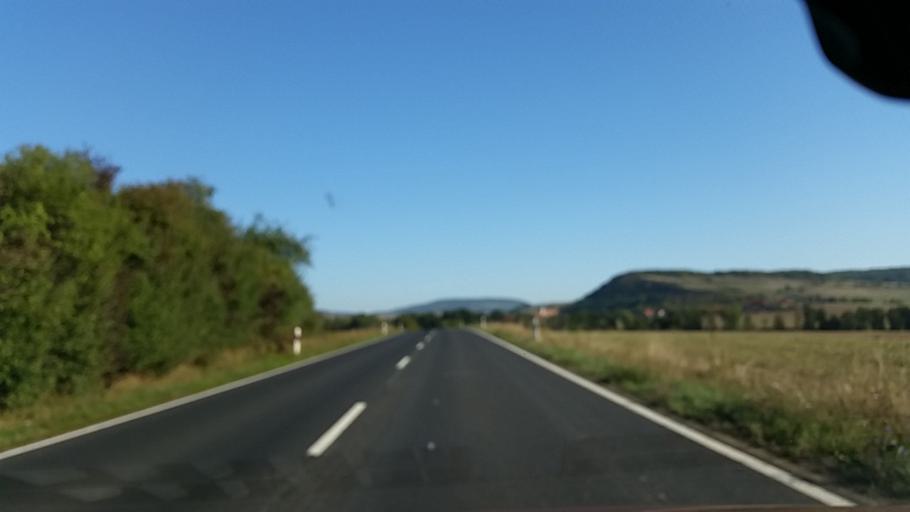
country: DE
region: Bavaria
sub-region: Regierungsbezirk Unterfranken
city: Gossenheim
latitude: 50.0312
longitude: 9.7799
